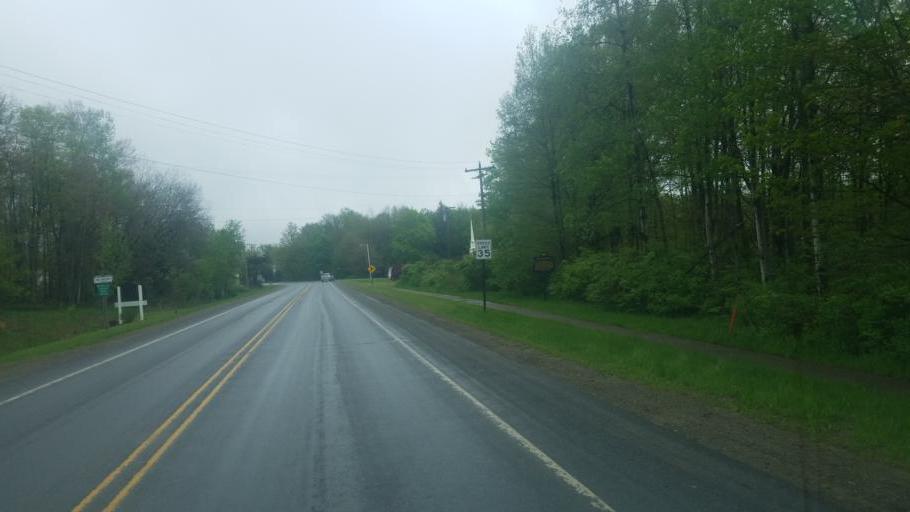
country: US
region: Pennsylvania
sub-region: McKean County
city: Kane
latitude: 41.6582
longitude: -78.8004
